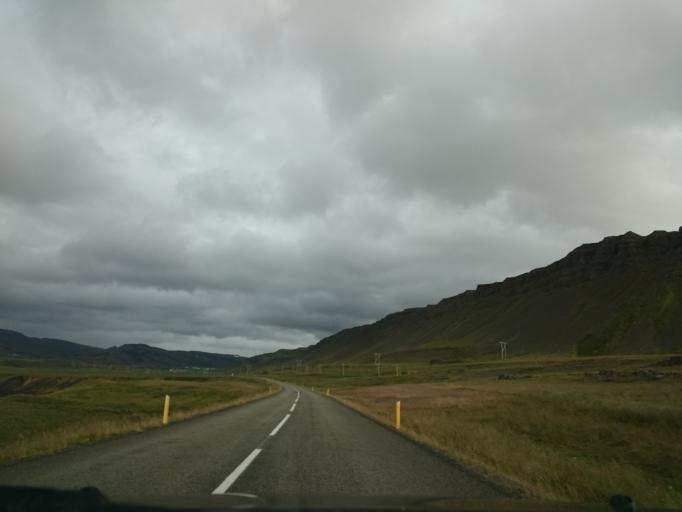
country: IS
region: West
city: Stykkisholmur
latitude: 65.4572
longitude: -21.9199
